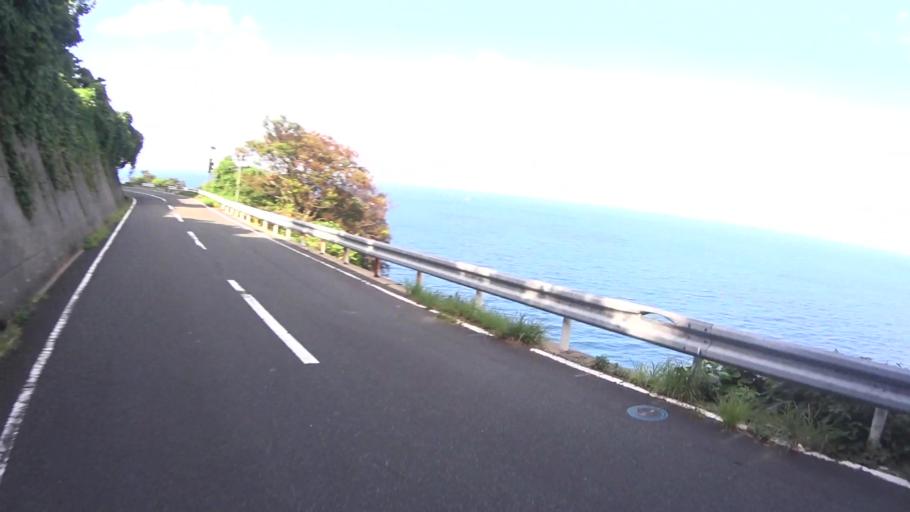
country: JP
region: Kyoto
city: Miyazu
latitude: 35.7632
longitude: 135.2386
